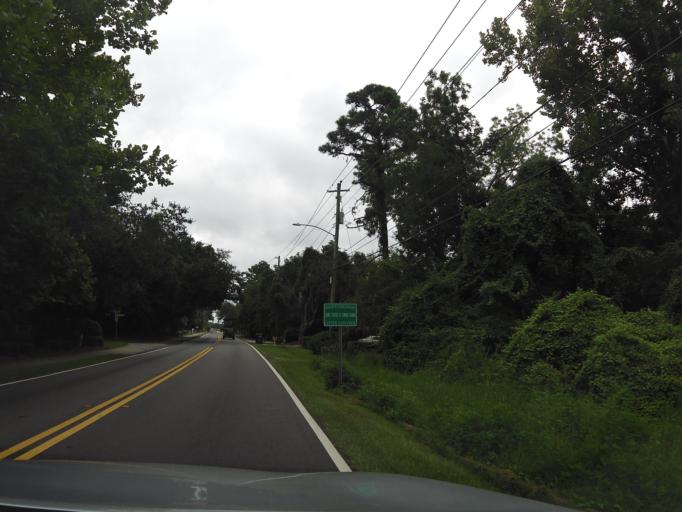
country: US
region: Georgia
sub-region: Glynn County
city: Saint Simon Mills
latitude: 31.1623
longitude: -81.3972
